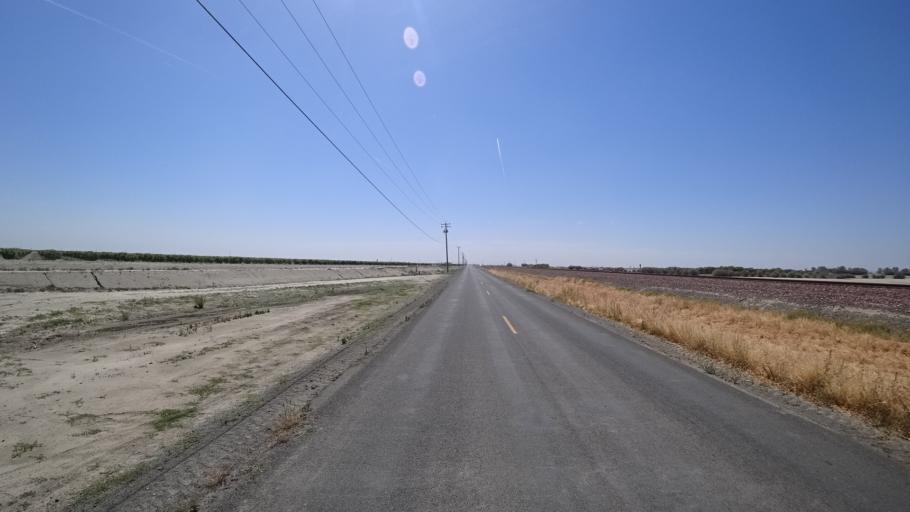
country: US
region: California
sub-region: Kings County
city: Corcoran
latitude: 36.0787
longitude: -119.5422
